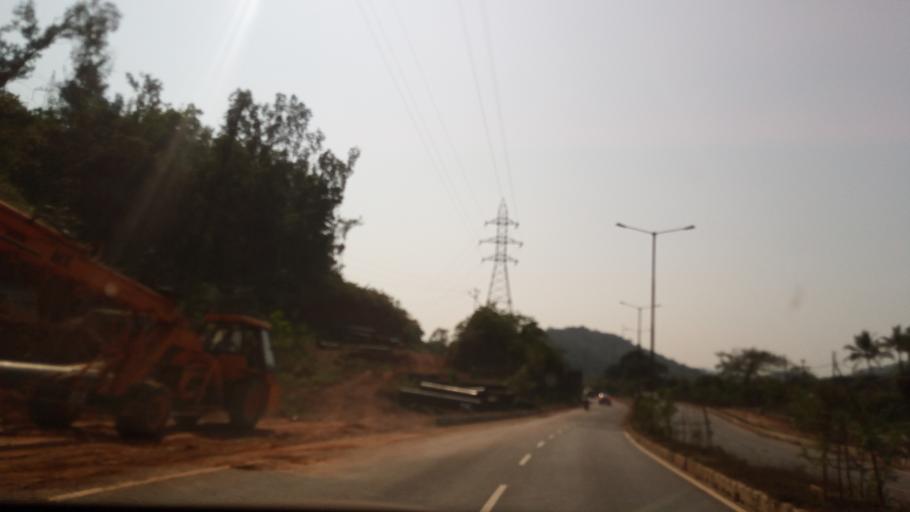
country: IN
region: Goa
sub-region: North Goa
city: Curti
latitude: 15.4134
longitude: 74.0318
